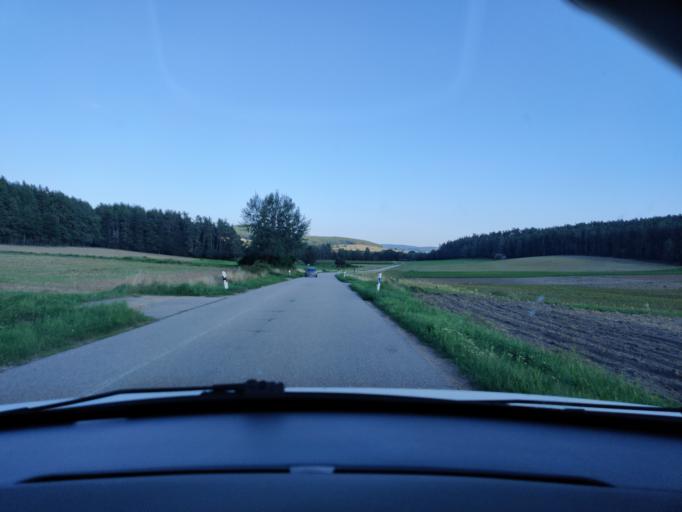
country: DE
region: Bavaria
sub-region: Upper Palatinate
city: Stulln
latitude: 49.4196
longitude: 12.1518
